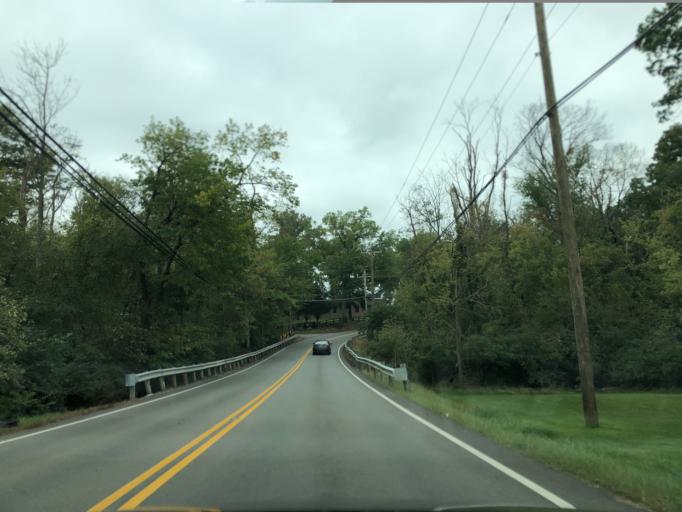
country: US
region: Ohio
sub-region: Warren County
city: Loveland Park
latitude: 39.2850
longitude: -84.2831
